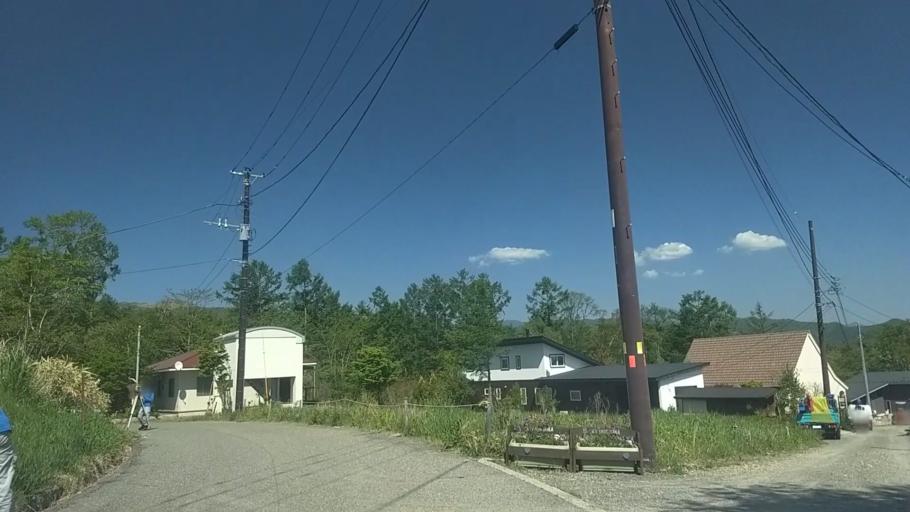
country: JP
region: Yamanashi
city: Nirasaki
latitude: 35.9043
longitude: 138.4355
